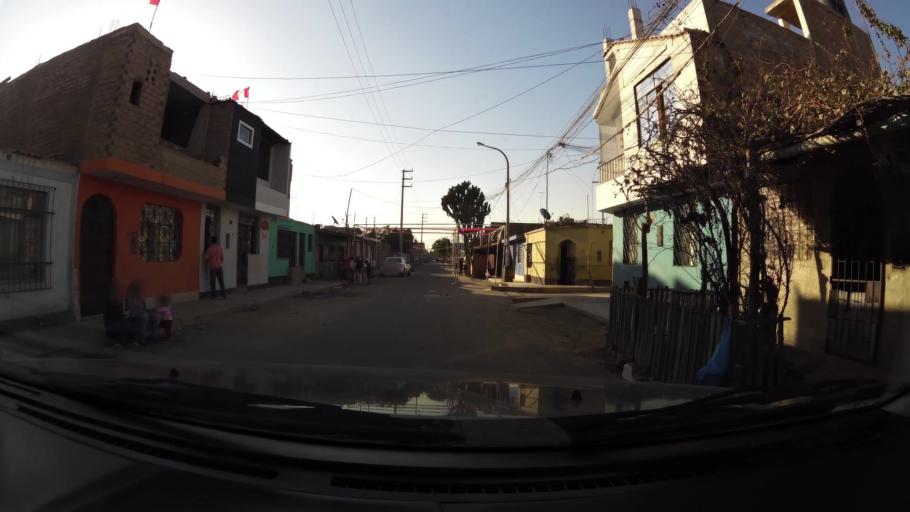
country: PE
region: Ica
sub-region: Provincia de Ica
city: Ica
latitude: -14.0658
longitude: -75.7207
